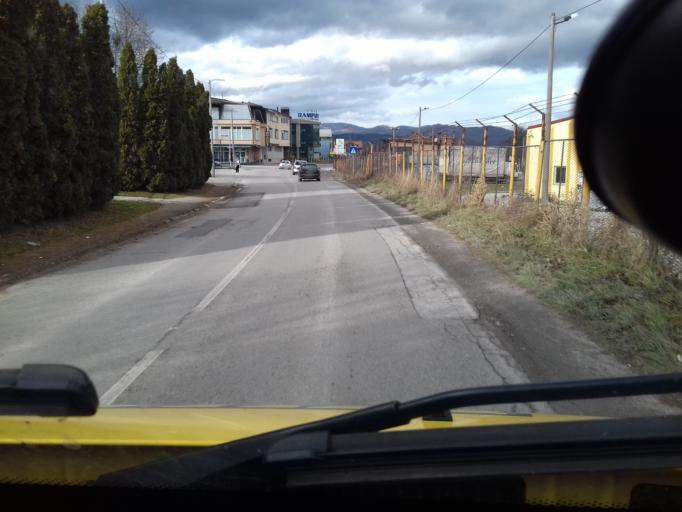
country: BA
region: Federation of Bosnia and Herzegovina
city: Gornje Mostre
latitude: 44.0021
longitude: 18.1579
